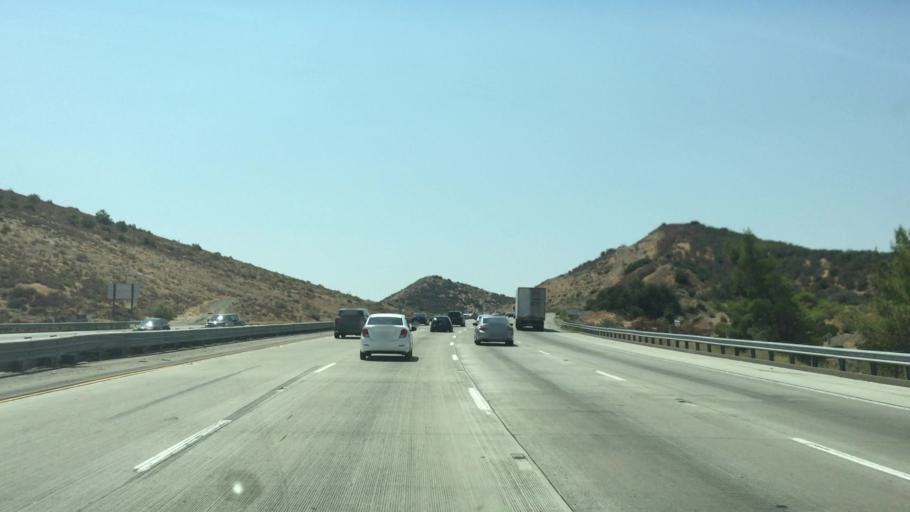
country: US
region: California
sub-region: Los Angeles County
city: Castaic
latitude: 34.6572
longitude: -118.7549
